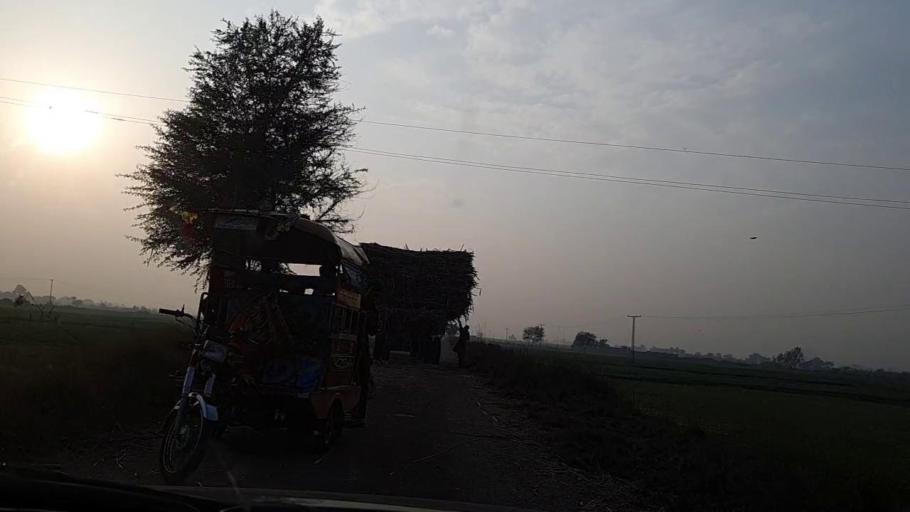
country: PK
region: Sindh
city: Nawabshah
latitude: 26.2980
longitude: 68.2632
